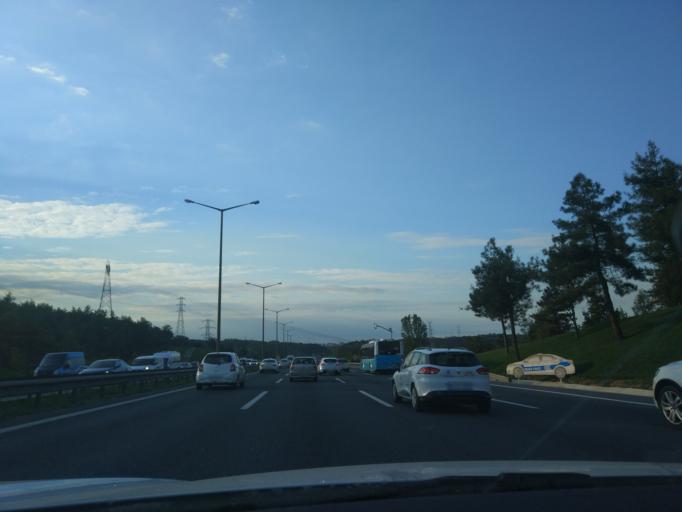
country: TR
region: Istanbul
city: Umraniye
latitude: 41.0707
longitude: 29.1060
